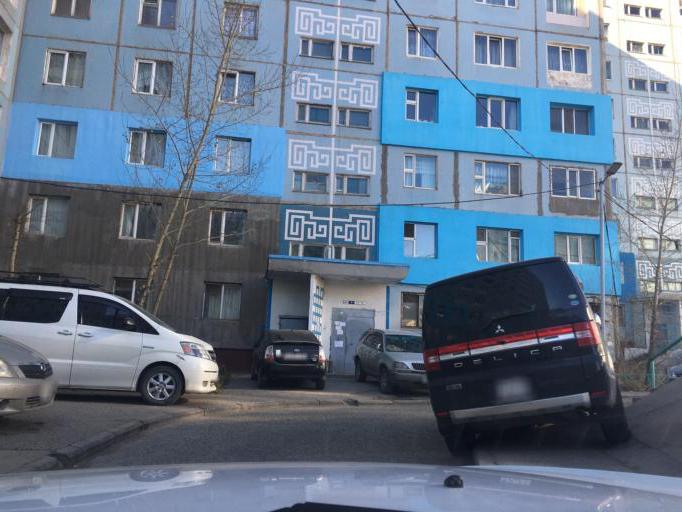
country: MN
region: Ulaanbaatar
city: Ulaanbaatar
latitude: 47.9205
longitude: 106.8651
